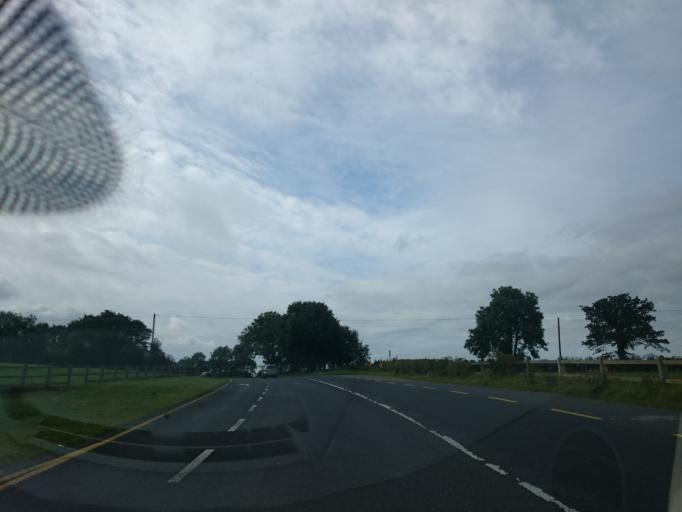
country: IE
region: Munster
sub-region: Waterford
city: Tra Mhor
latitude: 52.2084
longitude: -7.1954
